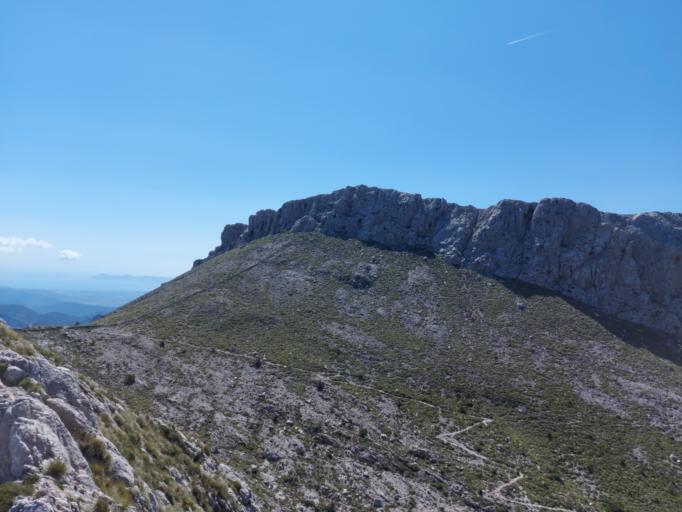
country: ES
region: Balearic Islands
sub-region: Illes Balears
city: Escorca
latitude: 39.8086
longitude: 2.8474
